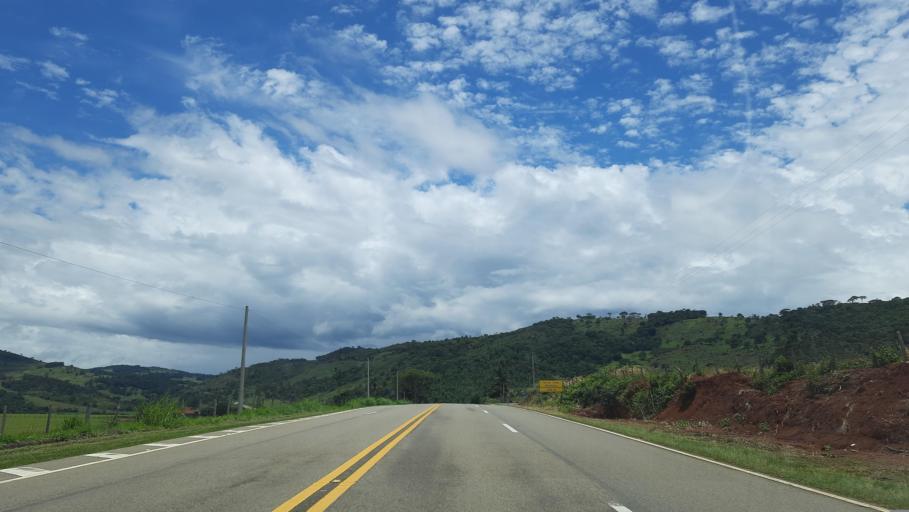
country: BR
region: Sao Paulo
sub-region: Vargem Grande Do Sul
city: Vargem Grande do Sul
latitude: -21.8240
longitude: -46.7805
